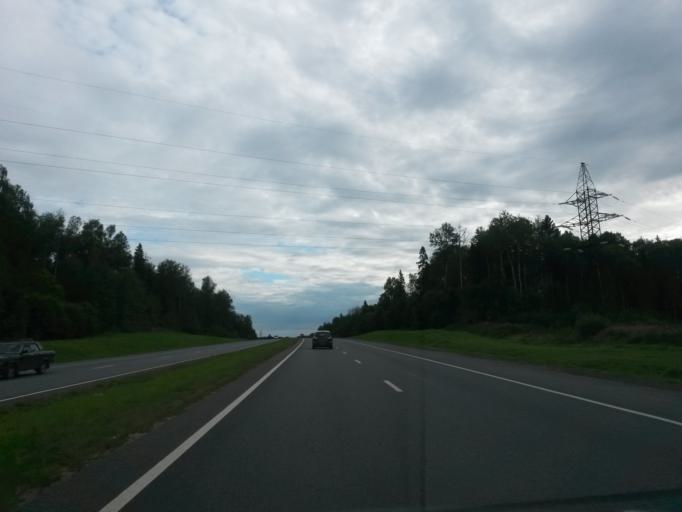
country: RU
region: Jaroslavl
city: Semibratovo
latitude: 57.3949
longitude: 39.6401
